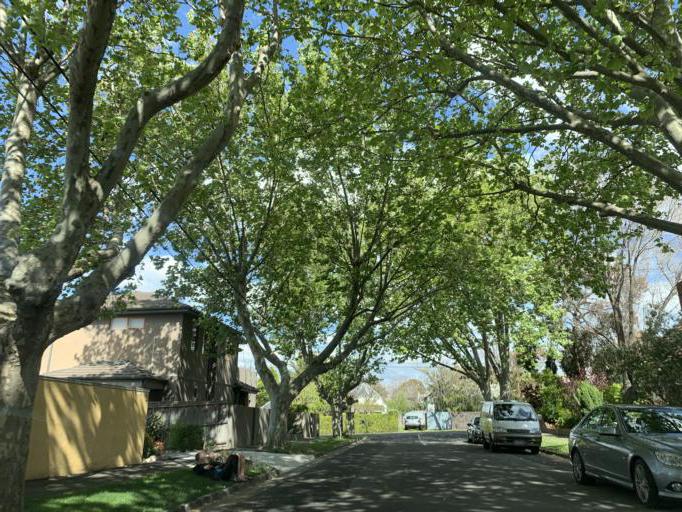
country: AU
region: Victoria
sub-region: Bayside
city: North Brighton
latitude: -37.9144
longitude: 144.9979
